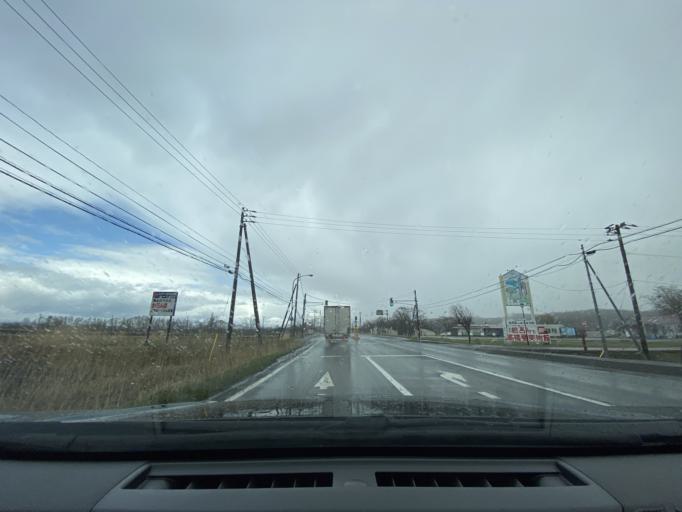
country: JP
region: Hokkaido
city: Fukagawa
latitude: 43.6707
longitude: 142.0146
